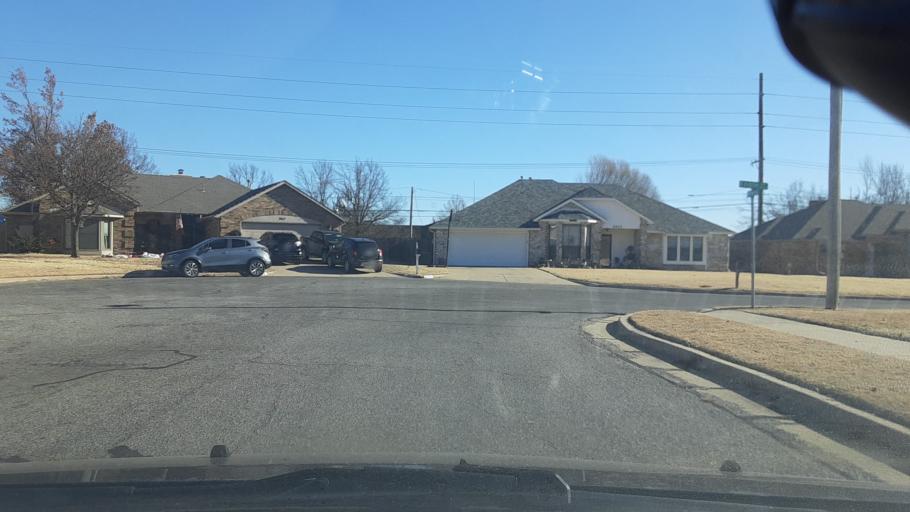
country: US
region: Oklahoma
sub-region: Kay County
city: Ponca City
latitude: 36.7310
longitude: -97.0861
